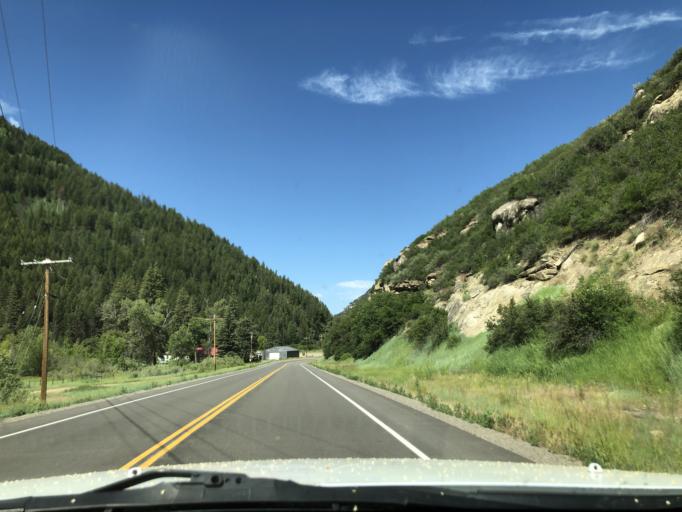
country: US
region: Colorado
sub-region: Delta County
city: Paonia
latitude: 38.9384
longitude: -107.3727
